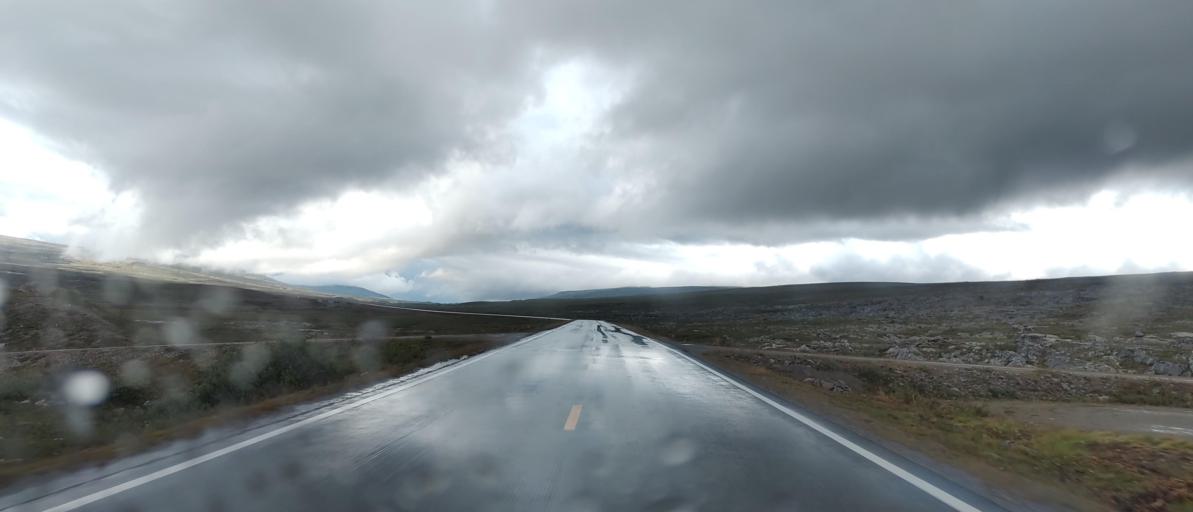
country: NO
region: Nordland
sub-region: Saltdal
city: Rognan
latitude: 66.5663
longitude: 15.3471
